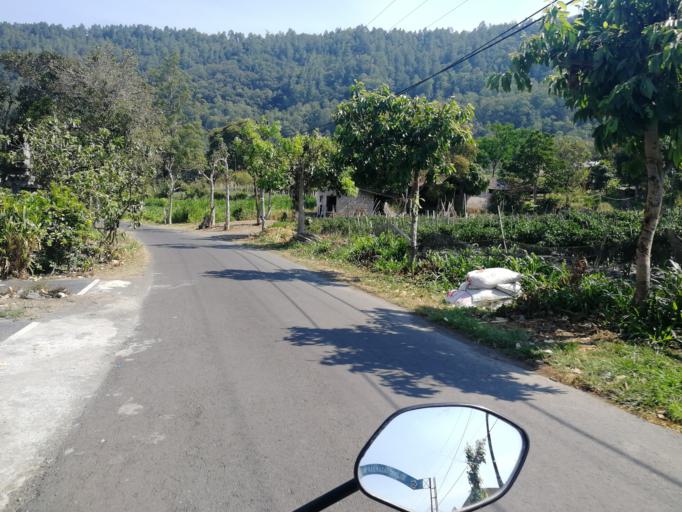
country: ID
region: Bali
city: Banjar Buahan
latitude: -8.2833
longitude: 115.3872
